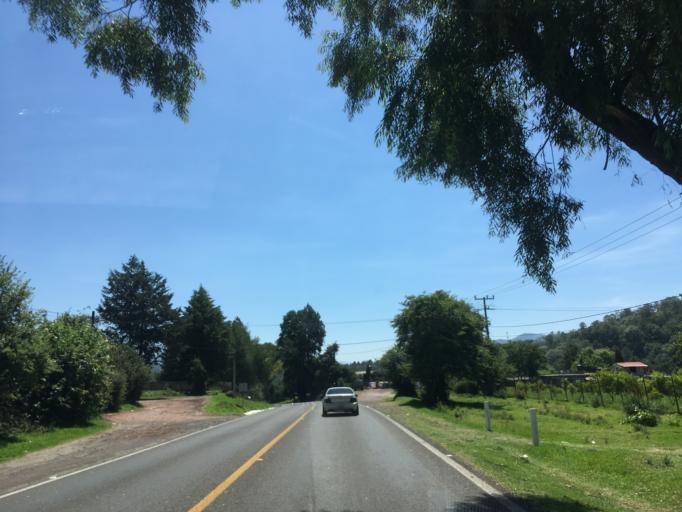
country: MX
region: Michoacan
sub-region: Hidalgo
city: San Lucas Huarirapeo (La Mesa de San Lucas)
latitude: 19.6673
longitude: -100.6735
